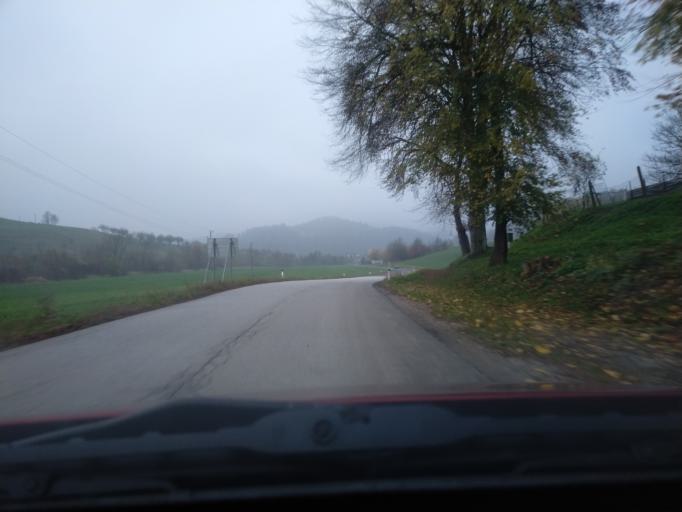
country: SI
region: Kungota
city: Zgornja Kungota
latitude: 46.6467
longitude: 15.6135
